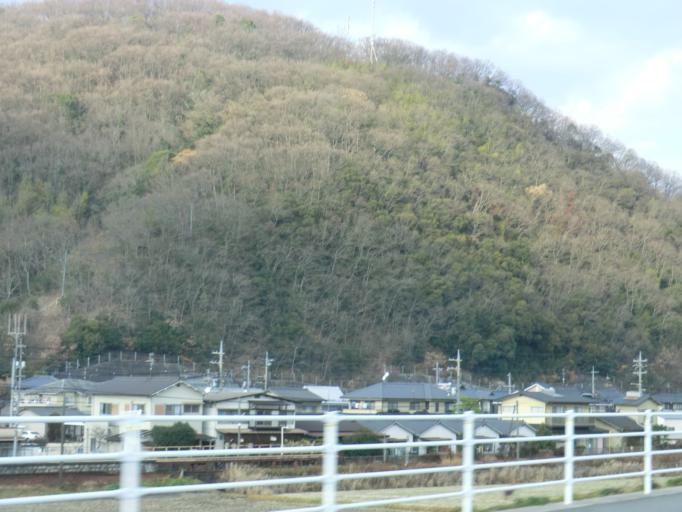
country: JP
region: Okayama
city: Okayama-shi
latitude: 34.7042
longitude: 133.9456
